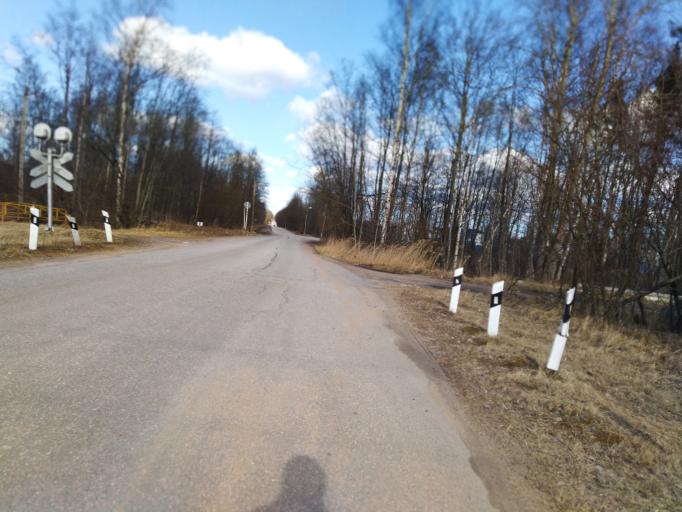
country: RU
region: Leningrad
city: Novoye Devyatkino
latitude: 60.0957
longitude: 30.4748
